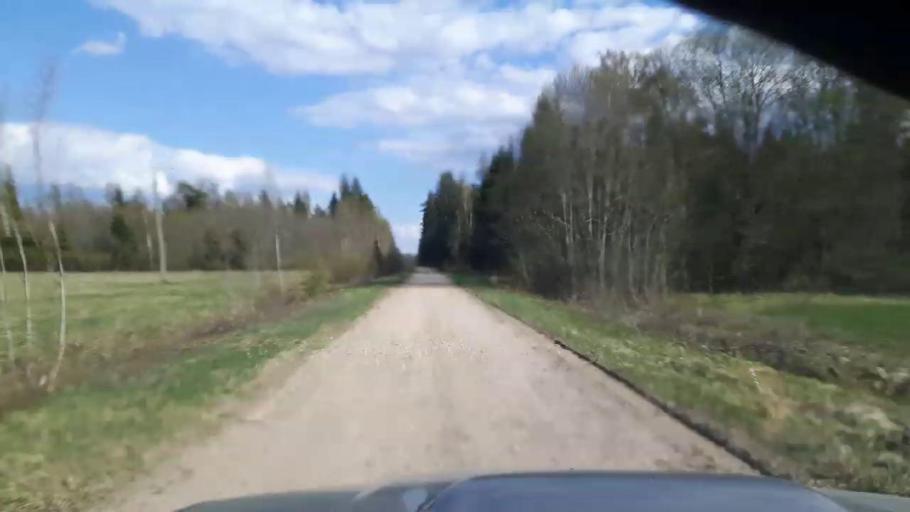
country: EE
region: Paernumaa
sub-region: Tootsi vald
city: Tootsi
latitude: 58.4469
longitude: 24.8671
